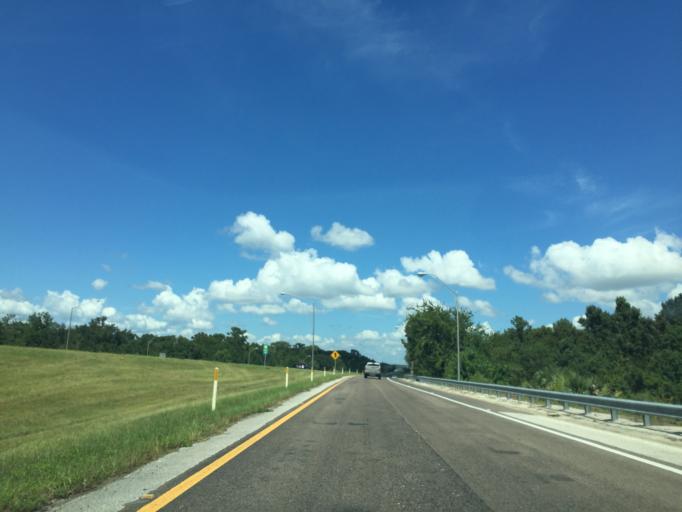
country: US
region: Florida
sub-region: Seminole County
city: Oviedo
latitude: 28.6929
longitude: -81.2283
